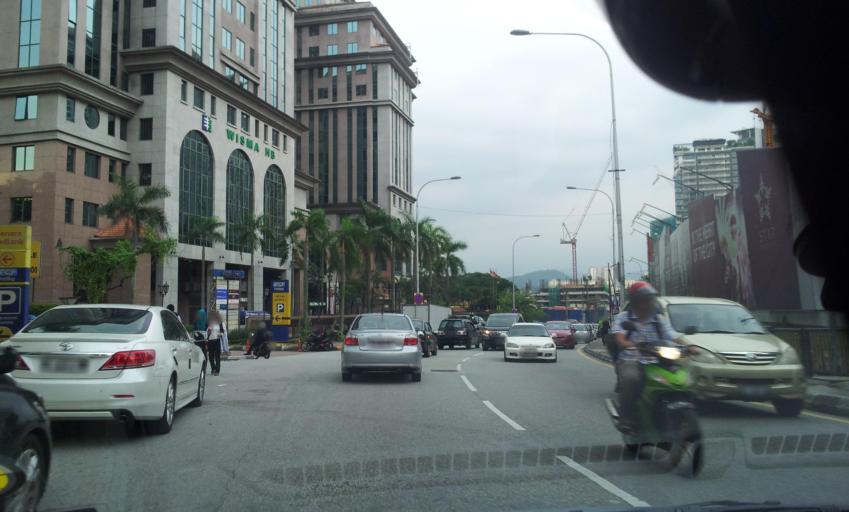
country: MY
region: Kuala Lumpur
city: Kuala Lumpur
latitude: 3.1611
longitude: 101.7115
